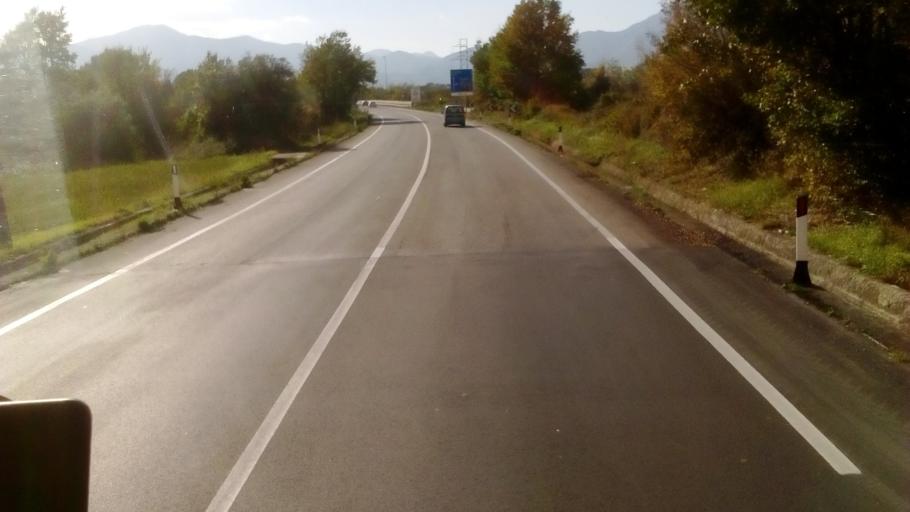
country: IT
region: Molise
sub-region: Provincia di Isernia
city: Taverna Ravindola
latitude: 41.5127
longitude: 14.1175
